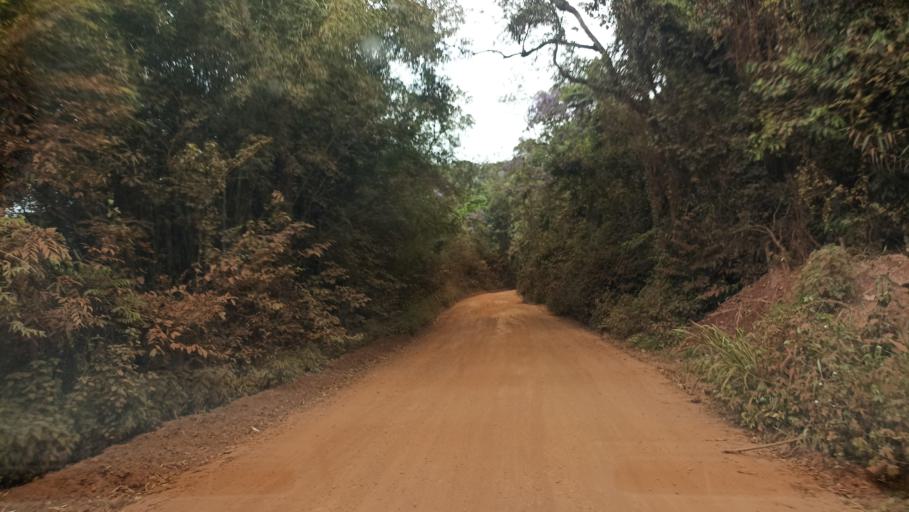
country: BR
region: Minas Gerais
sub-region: Itabirito
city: Itabirito
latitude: -20.3597
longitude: -43.7673
